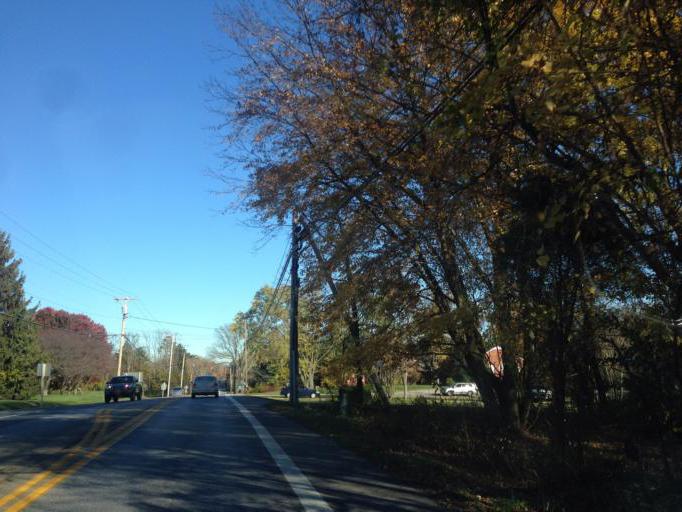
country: US
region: Maryland
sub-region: Howard County
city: Columbia
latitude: 39.2345
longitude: -76.8906
